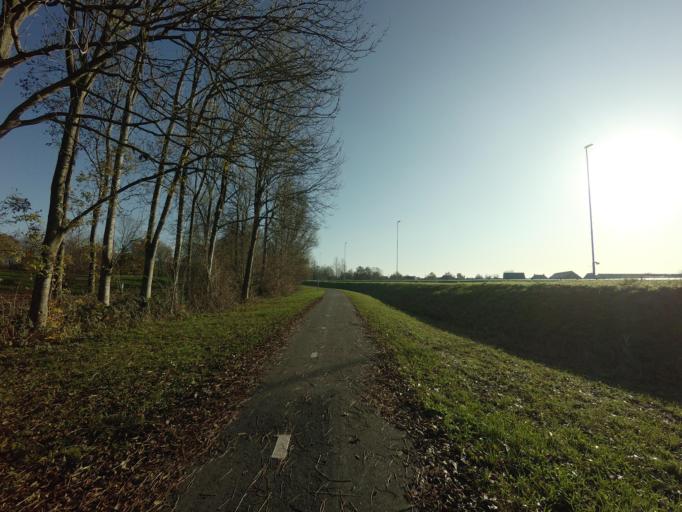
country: NL
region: Gelderland
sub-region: Gemeente Neerijnen
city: Neerijnen
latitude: 51.7791
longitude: 5.3283
